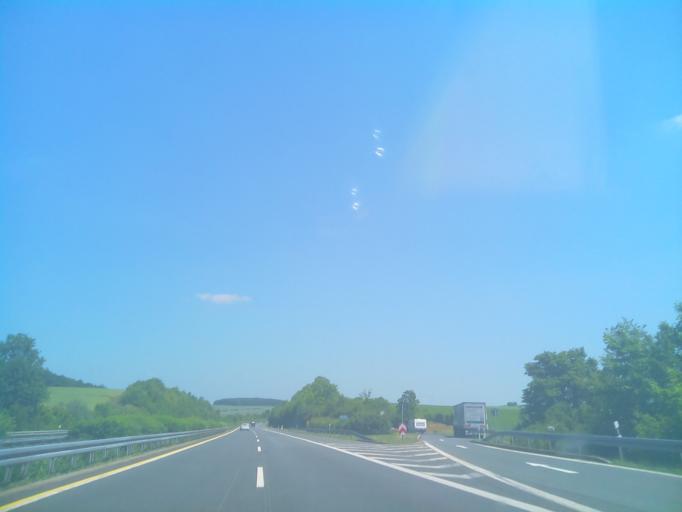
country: DE
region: Baden-Wuerttemberg
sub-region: Regierungsbezirk Stuttgart
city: Grossrinderfeld
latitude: 49.6703
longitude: 9.7705
